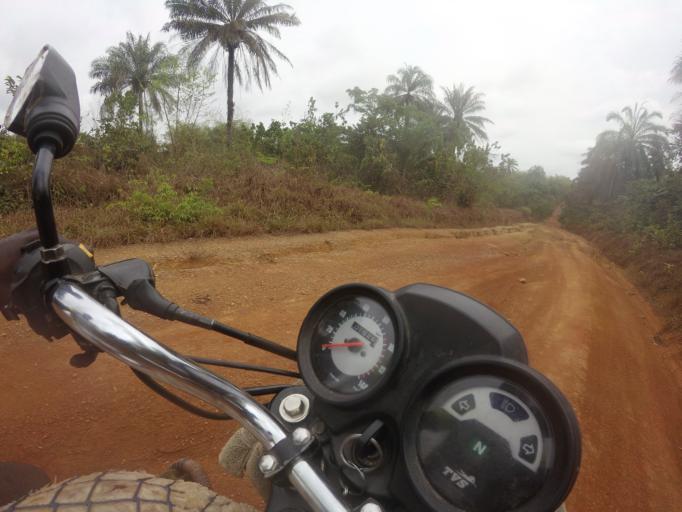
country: SL
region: Southern Province
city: Zimmi
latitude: 7.2102
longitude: -11.2024
